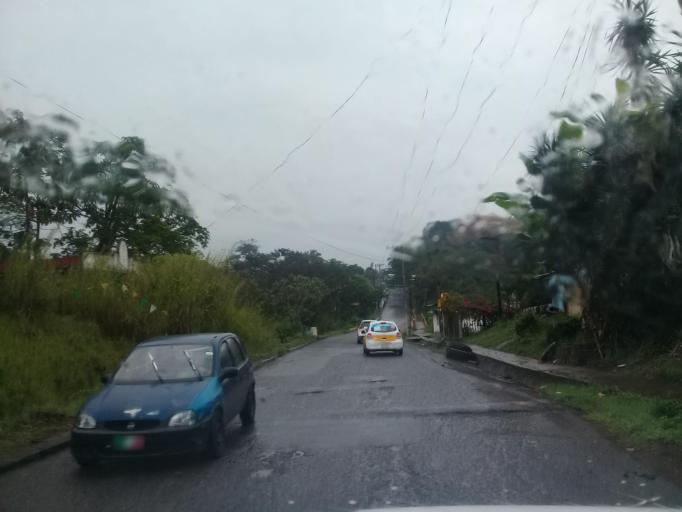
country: MX
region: Veracruz
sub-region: Cordoba
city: San Jose de Tapia
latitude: 18.8469
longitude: -96.9530
